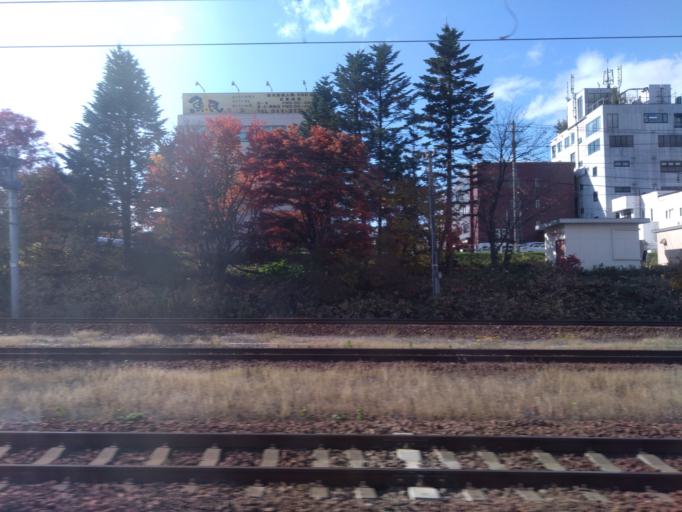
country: JP
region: Hokkaido
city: Kitahiroshima
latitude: 42.9798
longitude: 141.5632
